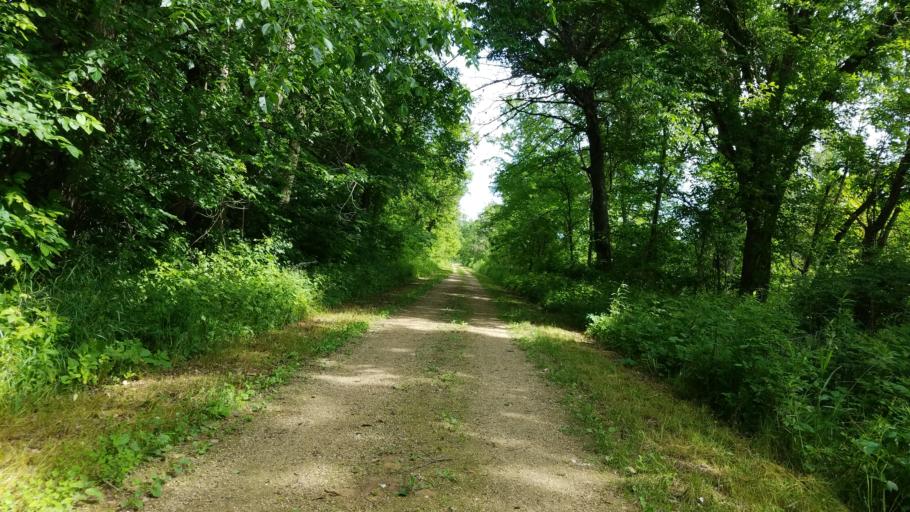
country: US
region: Wisconsin
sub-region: Dunn County
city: Menomonie
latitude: 44.7980
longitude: -91.9472
